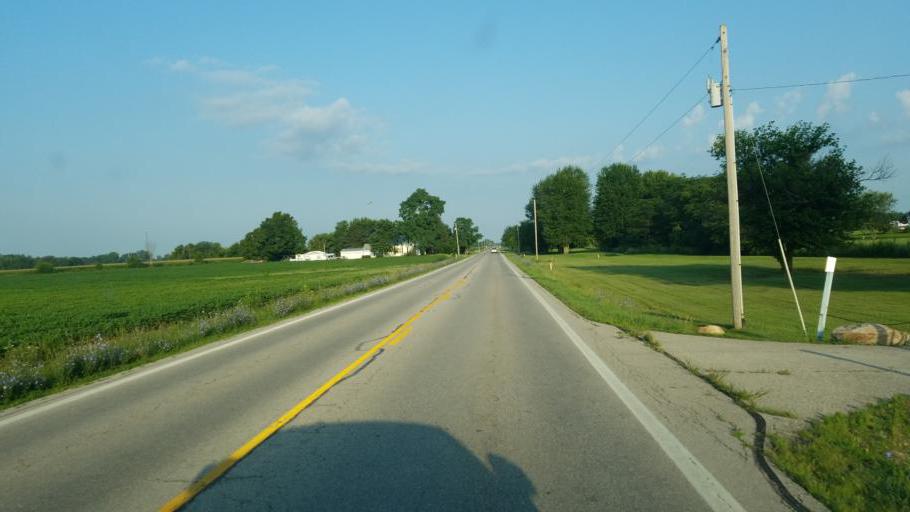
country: US
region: Ohio
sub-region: Morrow County
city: Cardington
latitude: 40.5870
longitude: -82.9484
